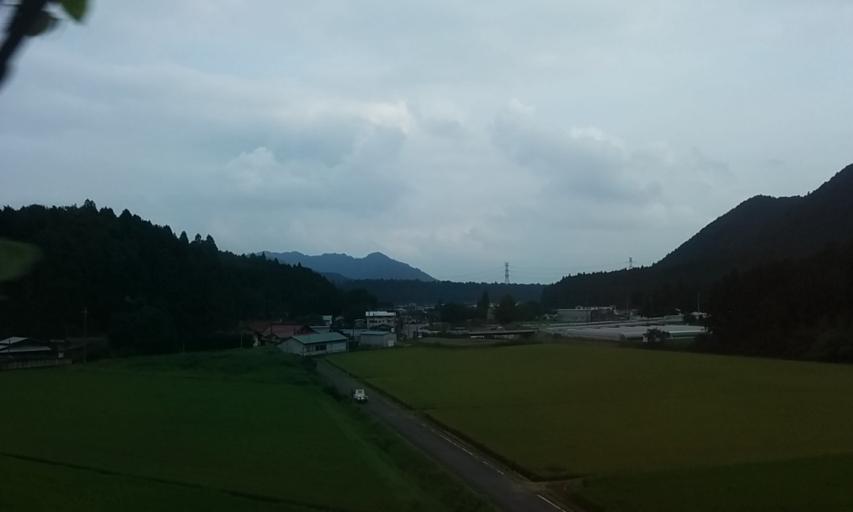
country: JP
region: Tochigi
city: Imaichi
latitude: 36.6475
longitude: 139.7117
